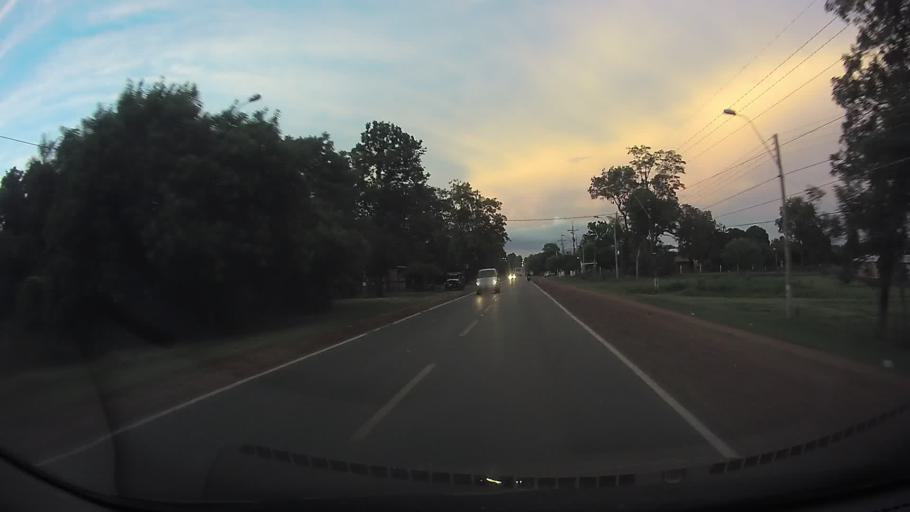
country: PY
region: Central
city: Ita
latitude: -25.4881
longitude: -57.3601
